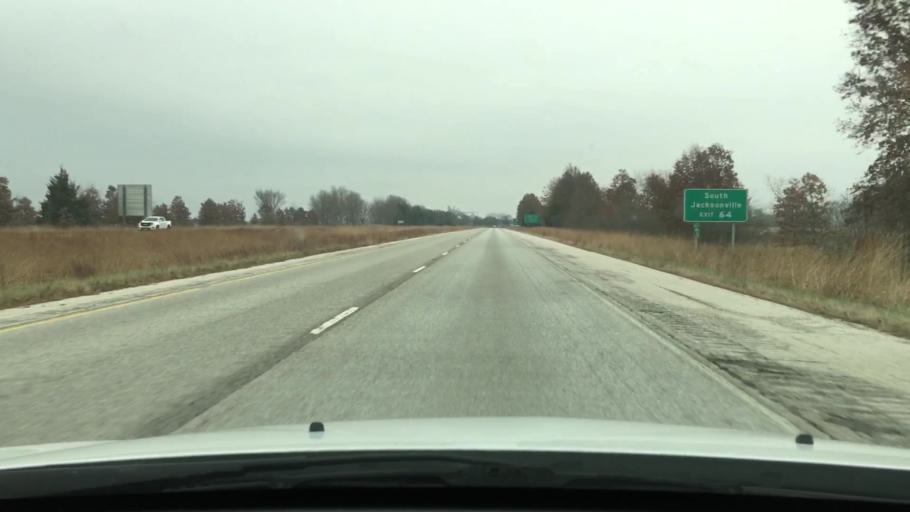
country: US
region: Illinois
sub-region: Morgan County
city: South Jacksonville
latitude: 39.6839
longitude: -90.2516
